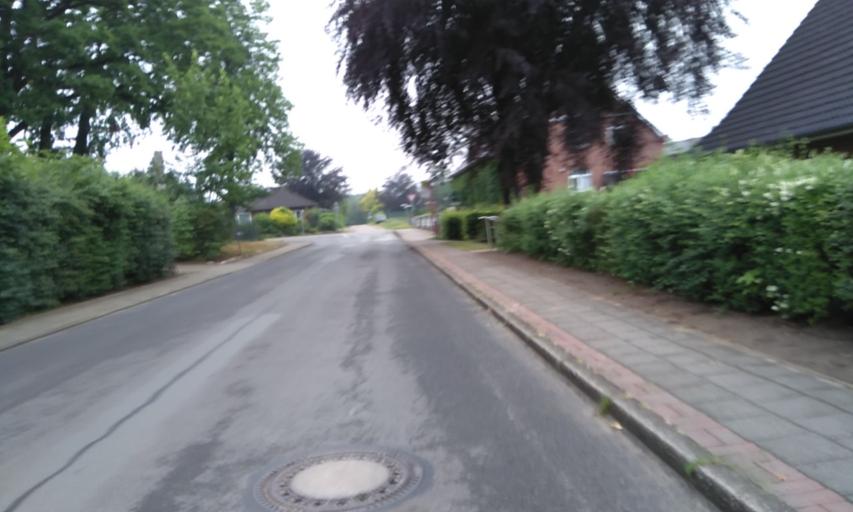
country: DE
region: Lower Saxony
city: Deinste
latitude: 53.5302
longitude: 9.4432
